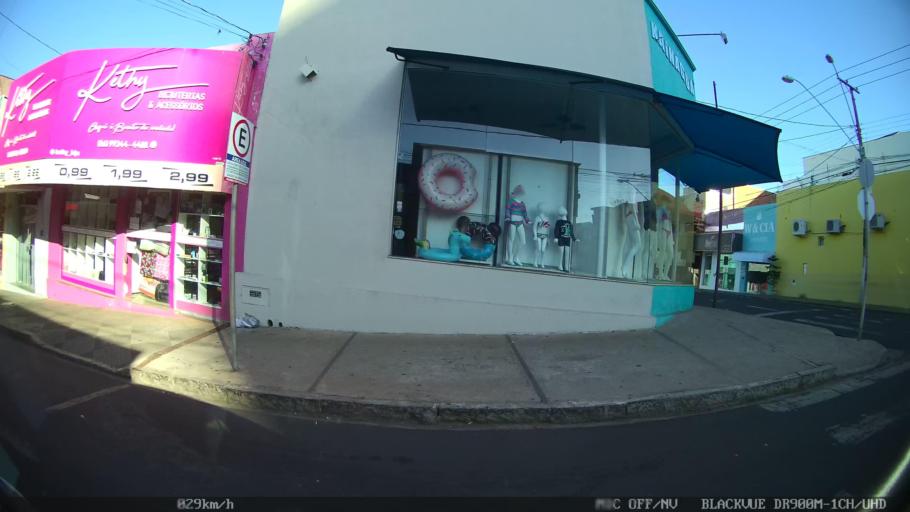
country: BR
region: Sao Paulo
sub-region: Olimpia
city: Olimpia
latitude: -20.7384
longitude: -48.9127
